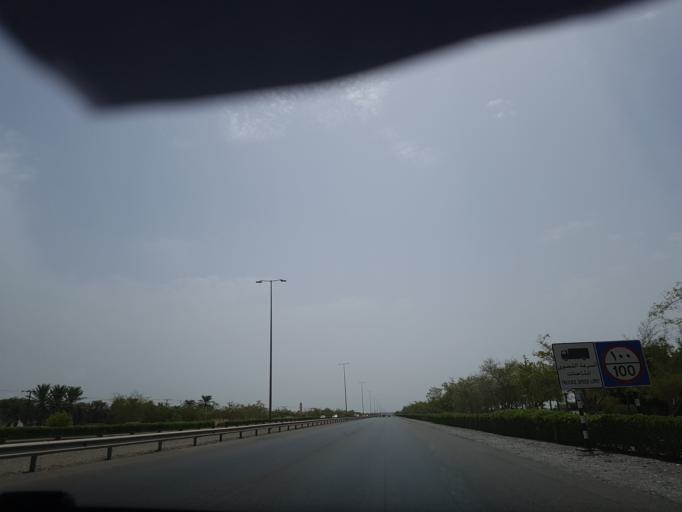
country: OM
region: Al Batinah
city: Barka'
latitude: 23.7313
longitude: 57.6977
